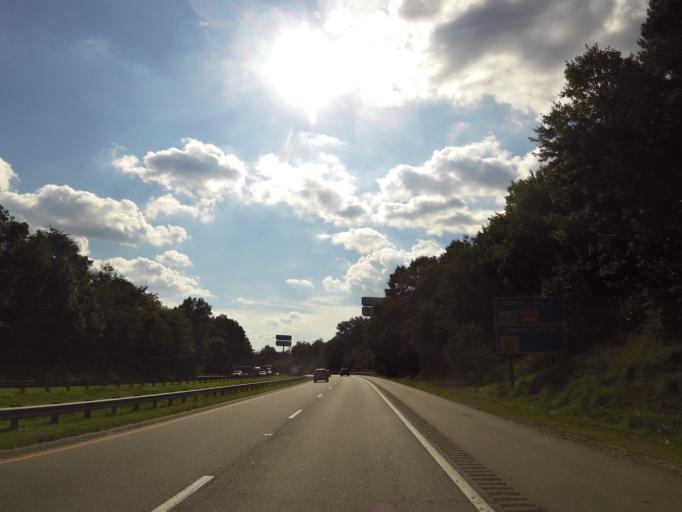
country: US
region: North Carolina
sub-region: Haywood County
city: Canton
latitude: 35.5501
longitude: -82.7388
